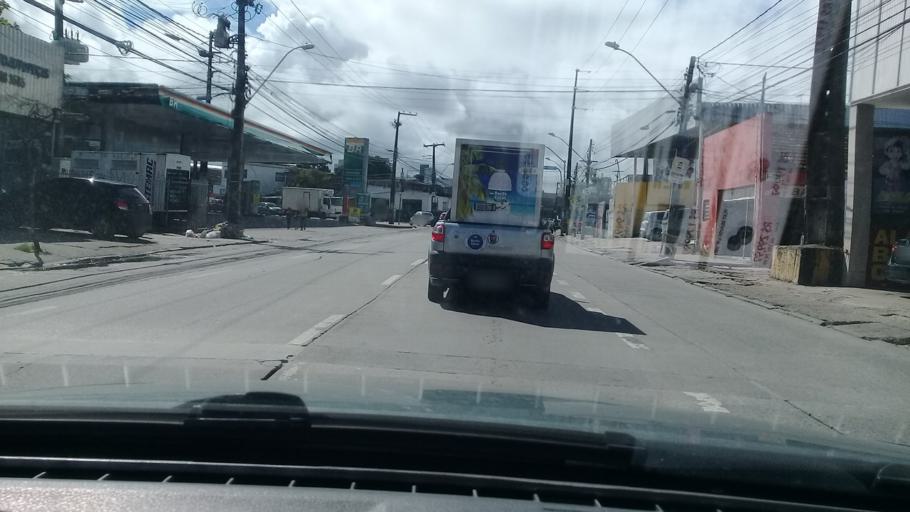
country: BR
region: Pernambuco
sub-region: Recife
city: Recife
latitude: -8.0697
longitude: -34.9084
